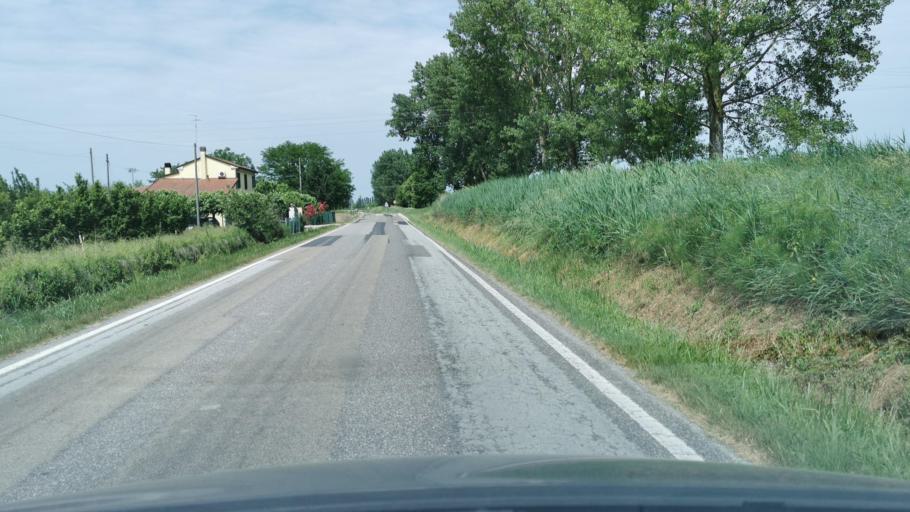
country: IT
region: Emilia-Romagna
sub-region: Provincia di Ravenna
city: Alfonsine
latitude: 44.4888
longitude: 12.0506
